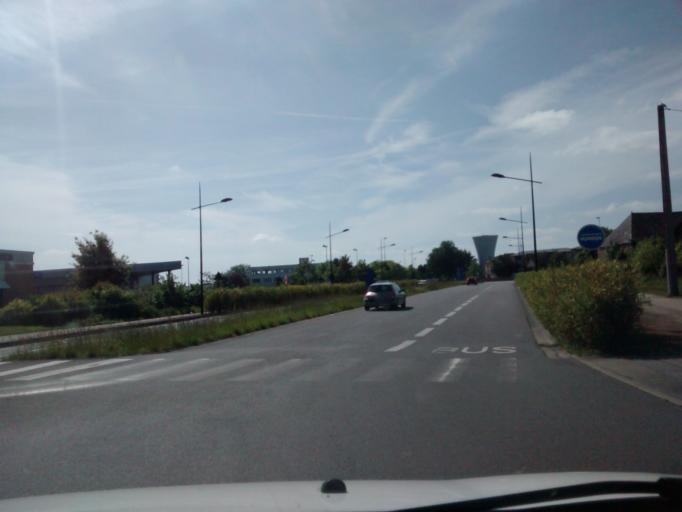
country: FR
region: Brittany
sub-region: Departement d'Ille-et-Vilaine
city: Pace
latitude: 48.1412
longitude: -1.7670
